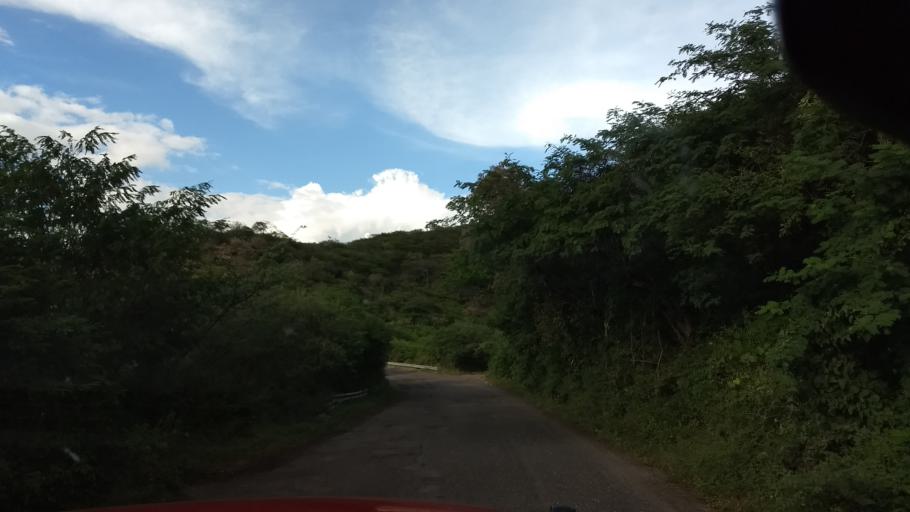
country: MX
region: Colima
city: Suchitlan
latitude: 19.4622
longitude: -103.8249
